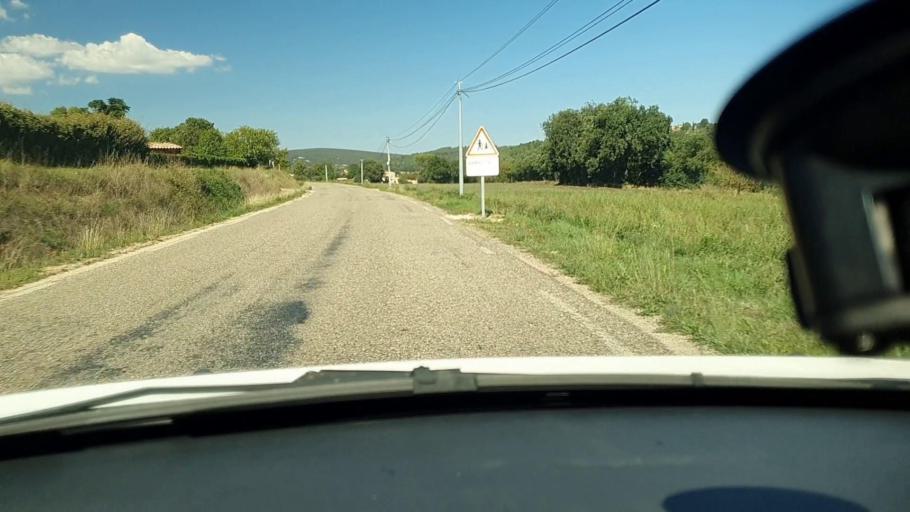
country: FR
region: Languedoc-Roussillon
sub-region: Departement du Gard
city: Goudargues
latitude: 44.1603
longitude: 4.4585
